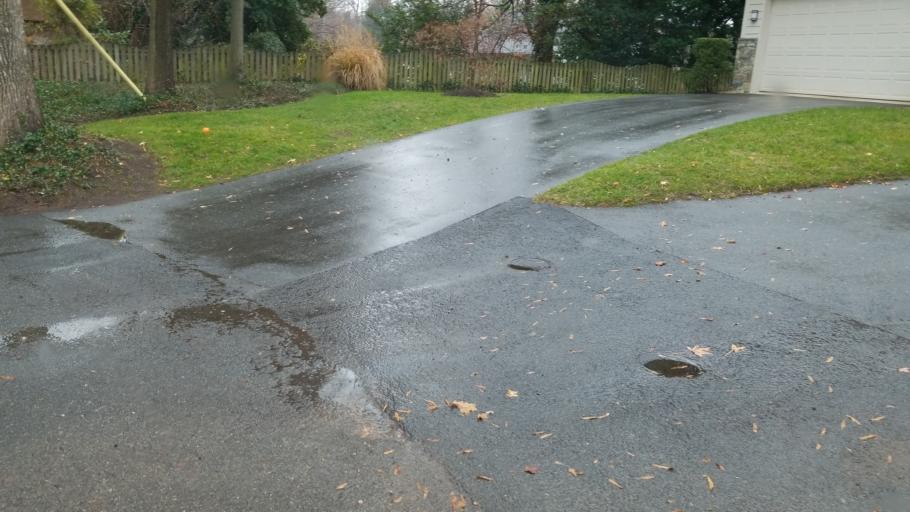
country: US
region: Maryland
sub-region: Montgomery County
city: Brookmont
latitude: 38.9253
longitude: -77.0990
